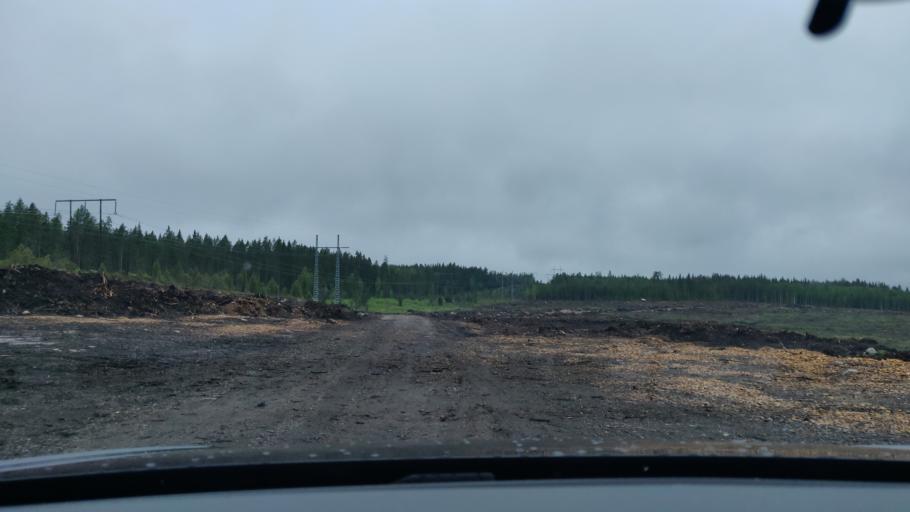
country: SE
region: Dalarna
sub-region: Avesta Kommun
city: Horndal
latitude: 60.3154
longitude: 16.3998
